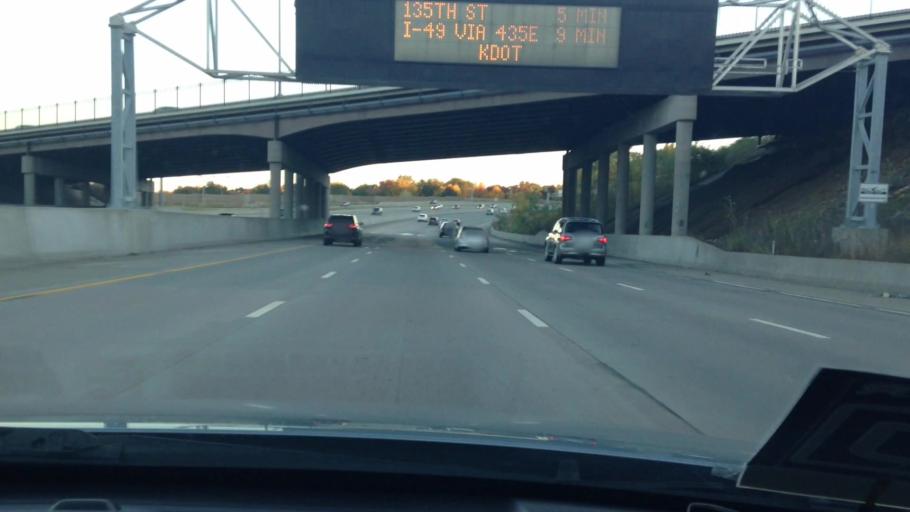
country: US
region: Kansas
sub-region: Johnson County
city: Lenexa
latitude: 38.9572
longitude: -94.7087
